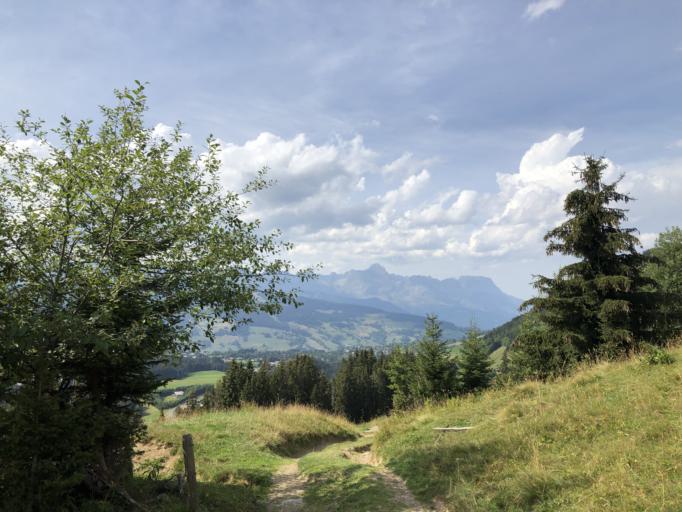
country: FR
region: Rhone-Alpes
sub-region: Departement de la Haute-Savoie
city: Megeve
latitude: 45.8255
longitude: 6.6536
